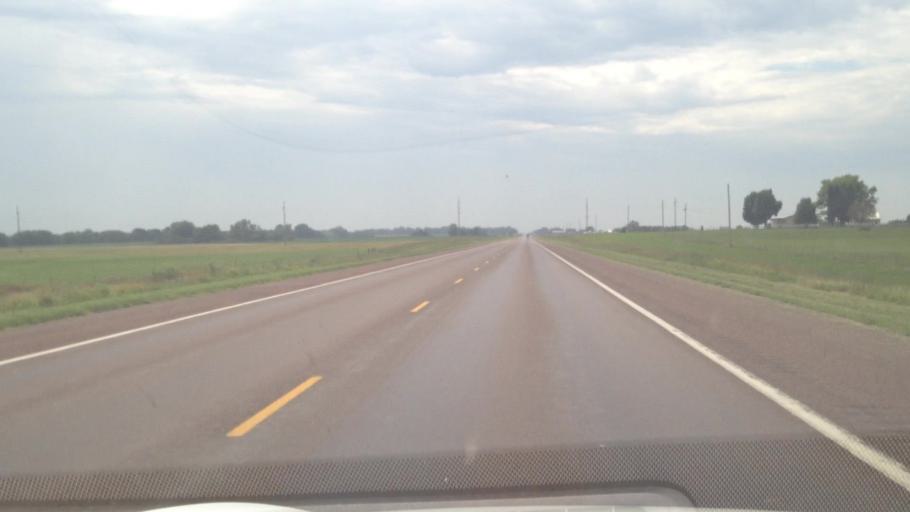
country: US
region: Kansas
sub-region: Crawford County
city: Girard
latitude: 37.4606
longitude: -94.8330
